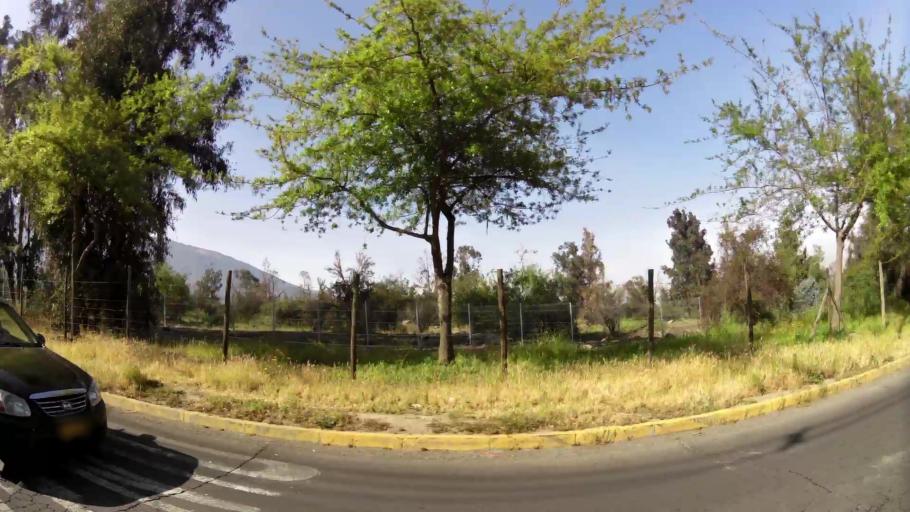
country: CL
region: Santiago Metropolitan
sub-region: Provincia de Santiago
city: Villa Presidente Frei, Nunoa, Santiago, Chile
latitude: -33.5010
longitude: -70.5370
